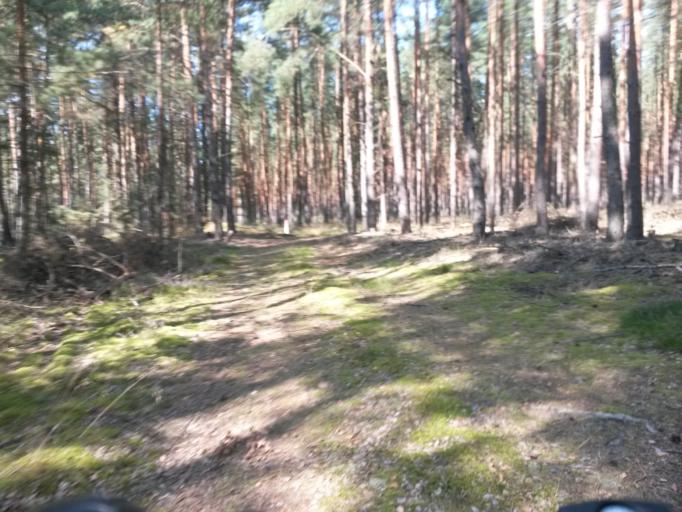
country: DE
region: Brandenburg
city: Milmersdorf
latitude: 53.0366
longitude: 13.5711
